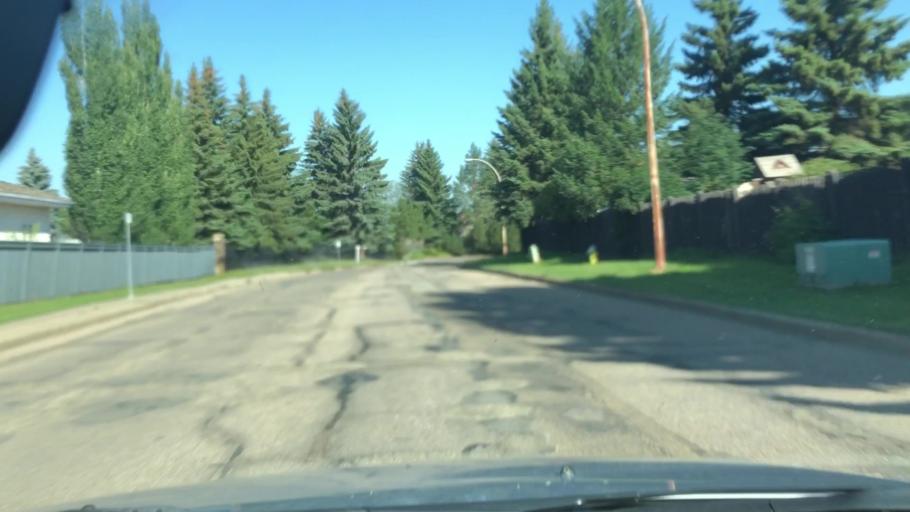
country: CA
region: Alberta
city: Edmonton
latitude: 53.4761
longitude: -113.6016
